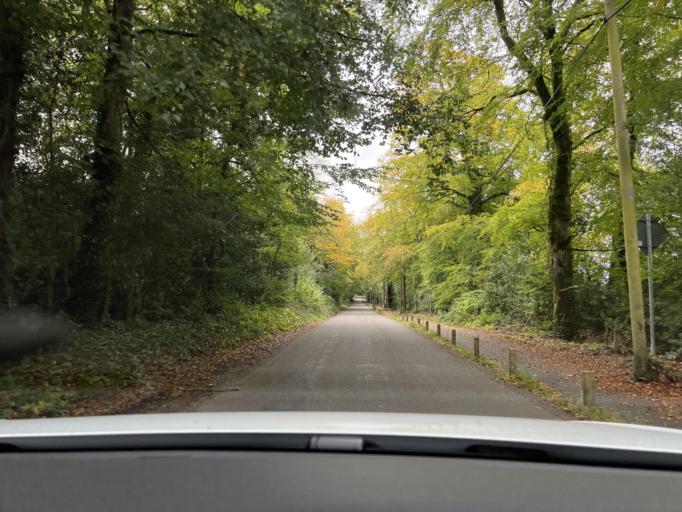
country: IE
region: Connaught
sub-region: Roscommon
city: Boyle
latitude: 53.9773
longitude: -8.2650
